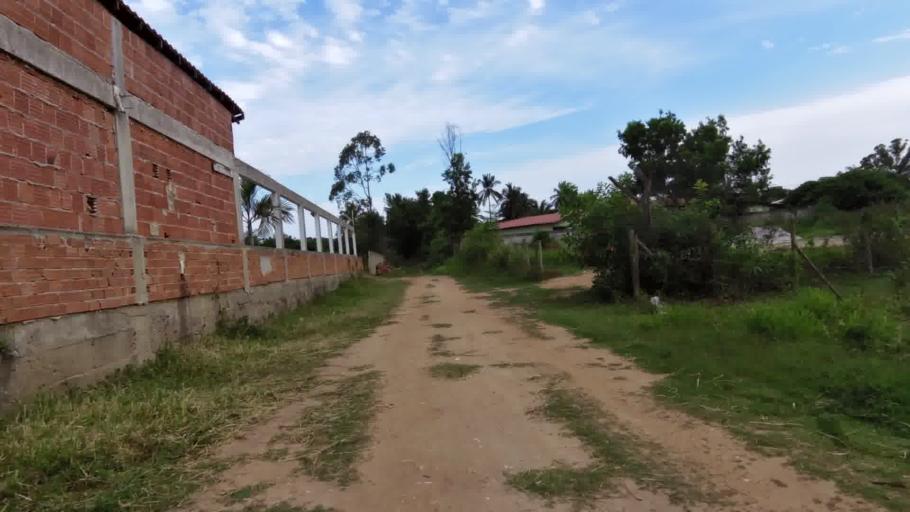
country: BR
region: Espirito Santo
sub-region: Piuma
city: Piuma
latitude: -20.8360
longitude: -40.7314
